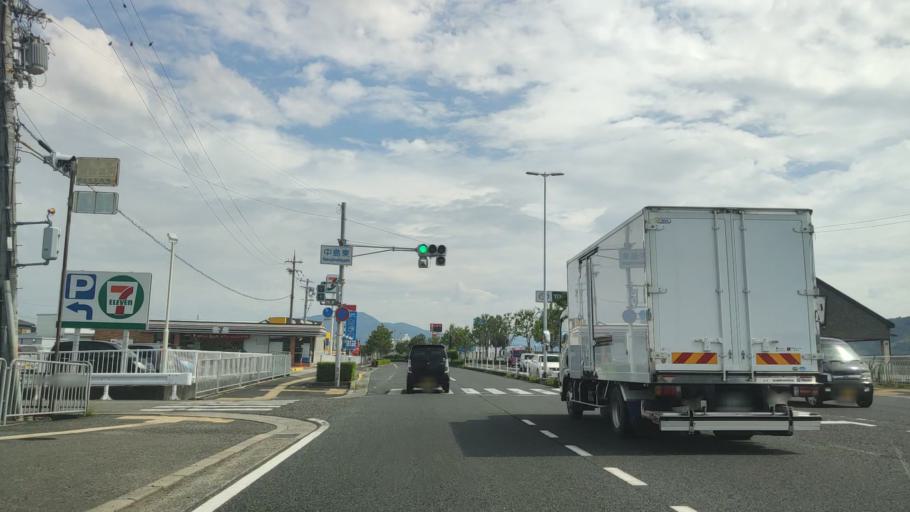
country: JP
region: Wakayama
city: Iwade
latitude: 34.2601
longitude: 135.2989
